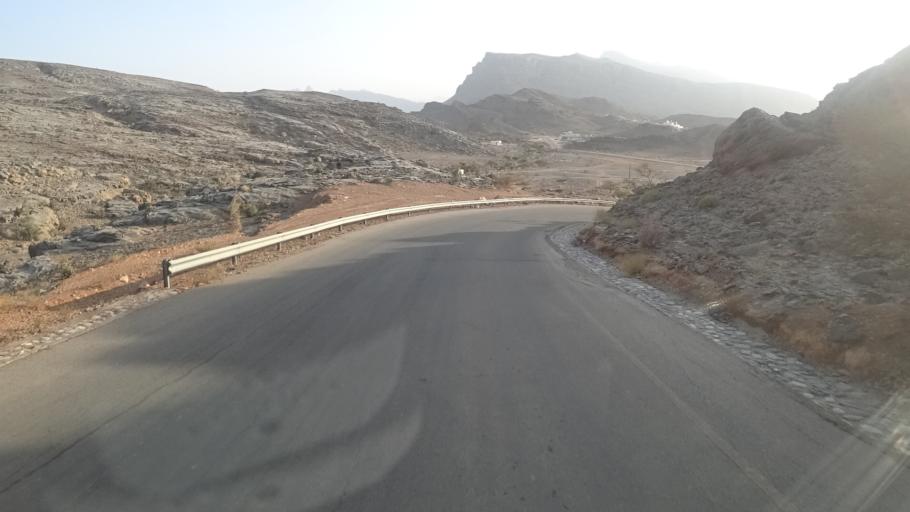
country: OM
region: Muhafazat ad Dakhiliyah
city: Bahla'
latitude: 23.2435
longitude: 57.1529
